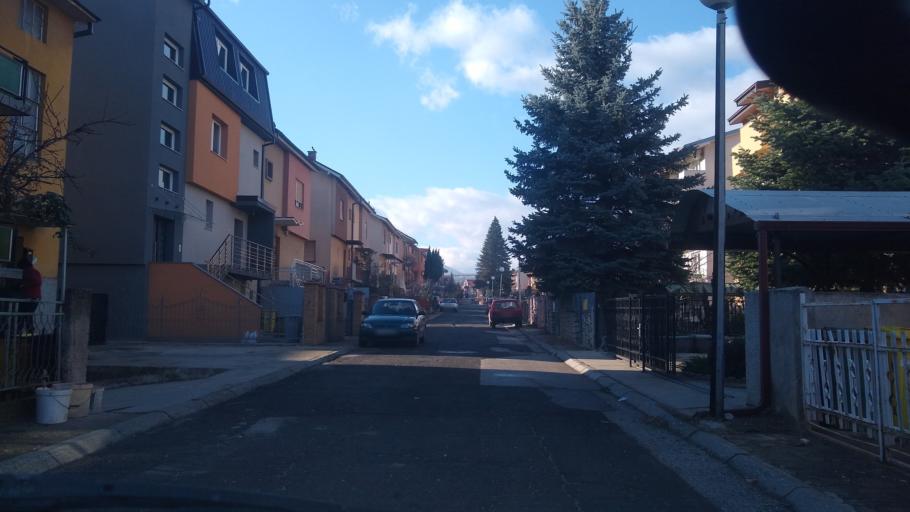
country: MK
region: Bitola
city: Bitola
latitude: 41.0217
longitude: 21.3243
